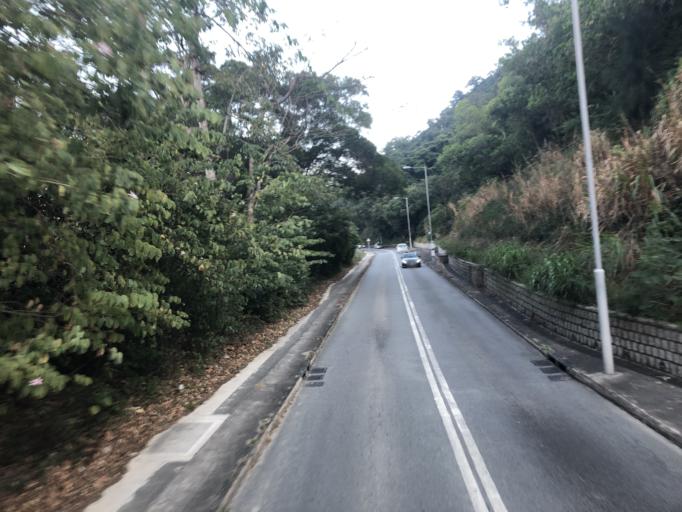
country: HK
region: Sai Kung
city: Sai Kung
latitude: 22.4150
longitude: 114.2678
